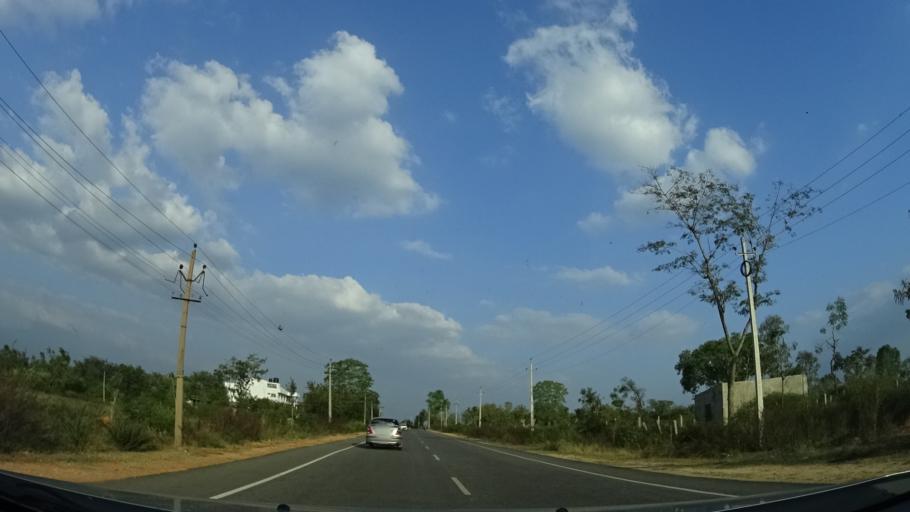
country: IN
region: Karnataka
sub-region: Mandya
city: Malavalli
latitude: 12.3717
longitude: 77.0231
